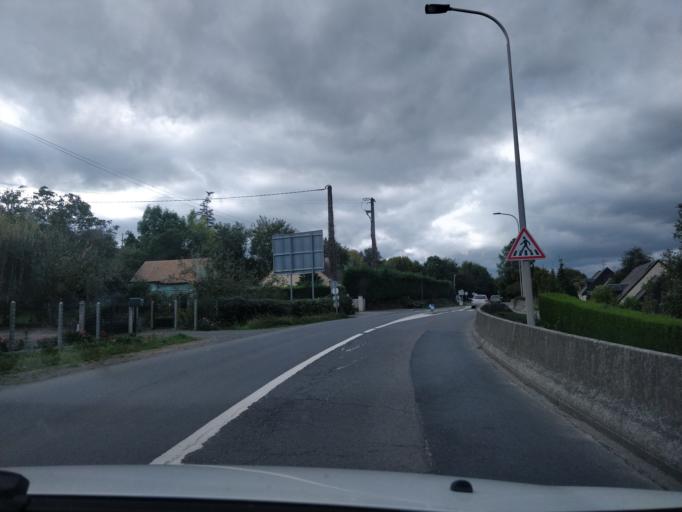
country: FR
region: Lower Normandy
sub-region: Departement du Calvados
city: Vire
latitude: 48.8453
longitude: -0.9049
